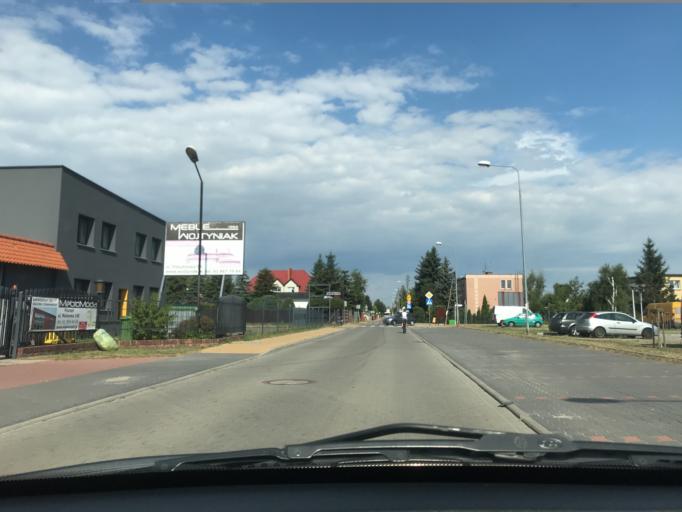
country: PL
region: Greater Poland Voivodeship
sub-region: Powiat poznanski
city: Plewiska
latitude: 52.3695
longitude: 16.8254
